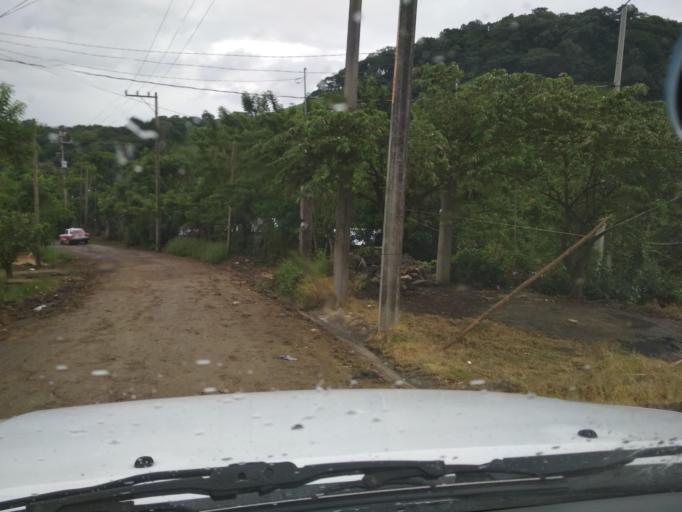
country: MX
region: Veracruz
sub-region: San Andres Tuxtla
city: San Isidro Xoteapan (San Isidro Texcaltitan)
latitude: 18.4651
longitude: -95.2375
